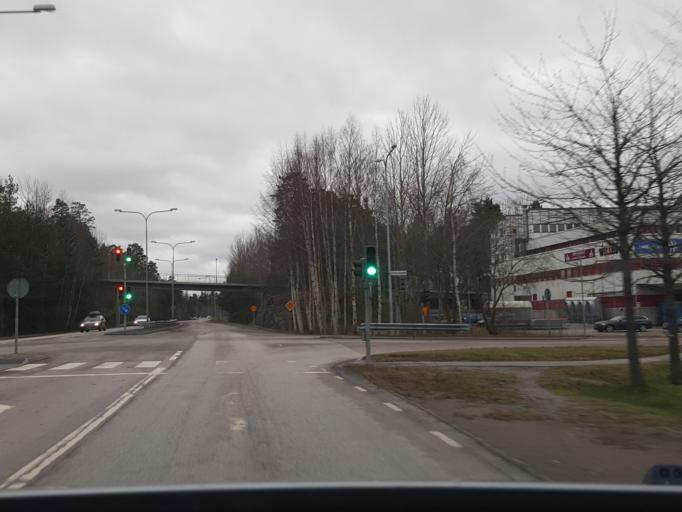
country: SE
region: Stockholm
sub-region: Nacka Kommun
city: Boo
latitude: 59.3269
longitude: 18.2610
